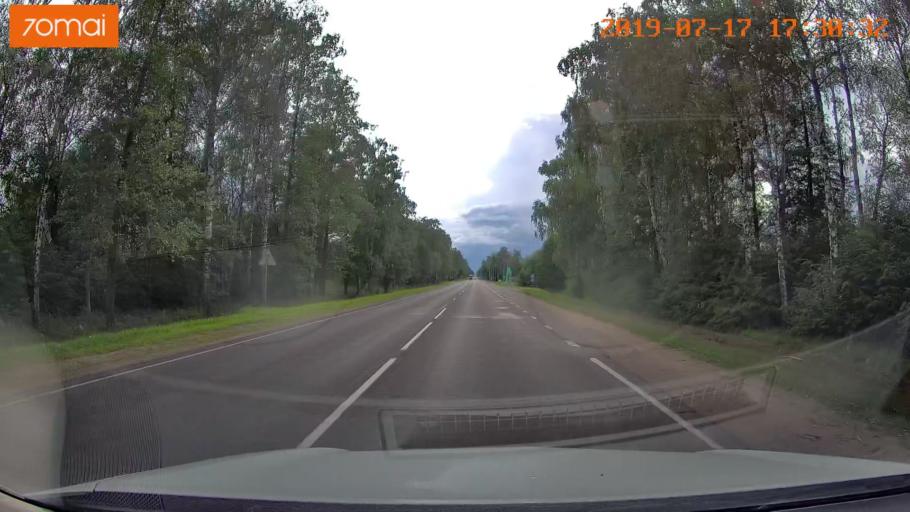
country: BY
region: Mogilev
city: Babruysk
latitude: 53.1191
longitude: 29.1409
